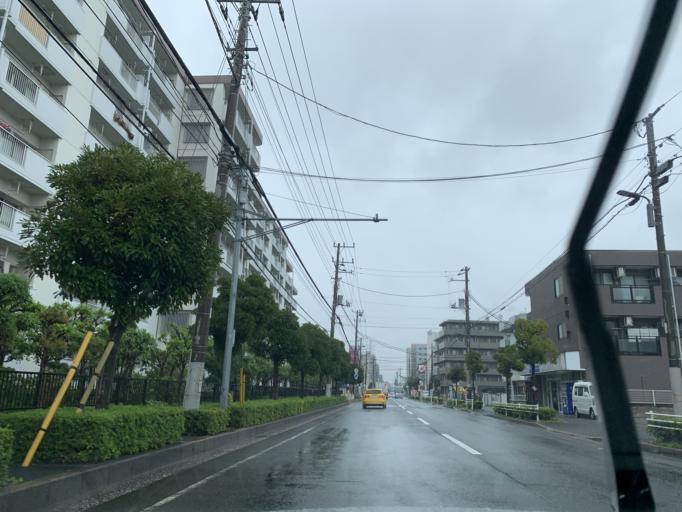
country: JP
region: Tokyo
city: Urayasu
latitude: 35.6666
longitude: 139.9045
